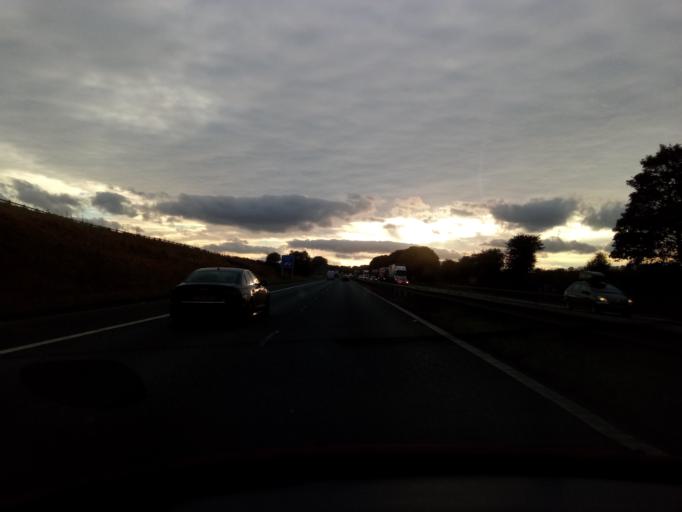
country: GB
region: England
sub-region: Darlington
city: High Coniscliffe
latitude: 54.4751
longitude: -1.6566
